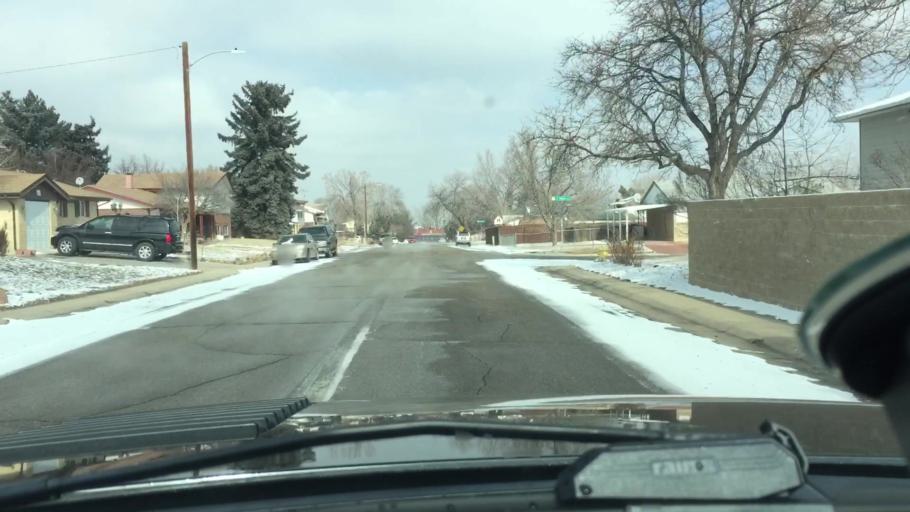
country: US
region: Colorado
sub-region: Adams County
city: Northglenn
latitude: 39.8812
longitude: -105.0056
